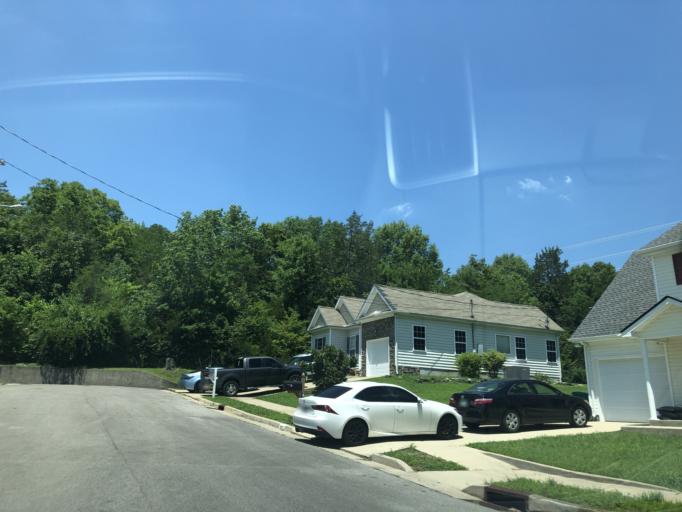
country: US
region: Tennessee
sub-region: Williamson County
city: Nolensville
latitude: 36.0106
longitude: -86.6548
